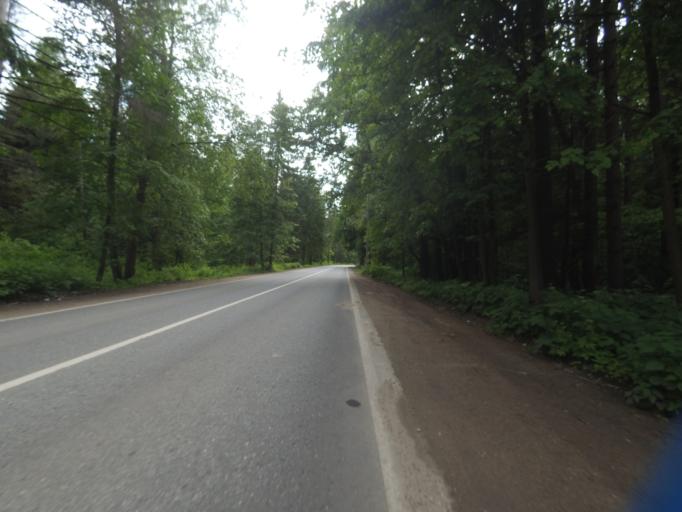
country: RU
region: Moskovskaya
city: Marfino
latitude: 56.0809
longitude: 37.5794
